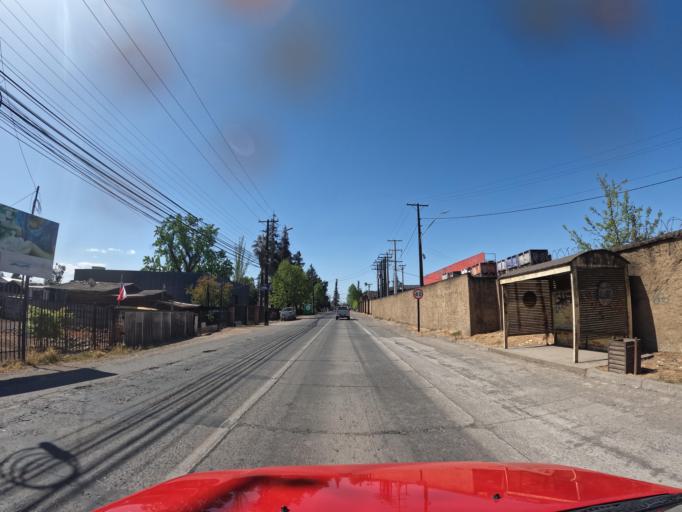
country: CL
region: Maule
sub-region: Provincia de Curico
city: Molina
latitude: -35.0793
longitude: -71.2612
